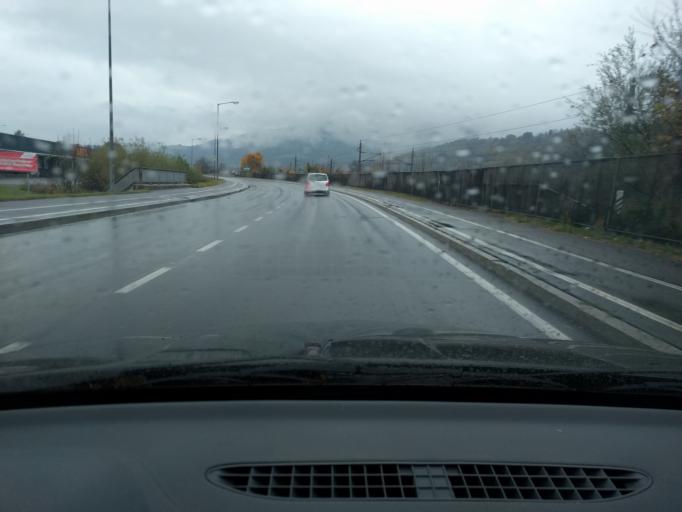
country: AT
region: Styria
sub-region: Politischer Bezirk Leoben
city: Proleb
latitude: 47.3854
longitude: 15.1220
